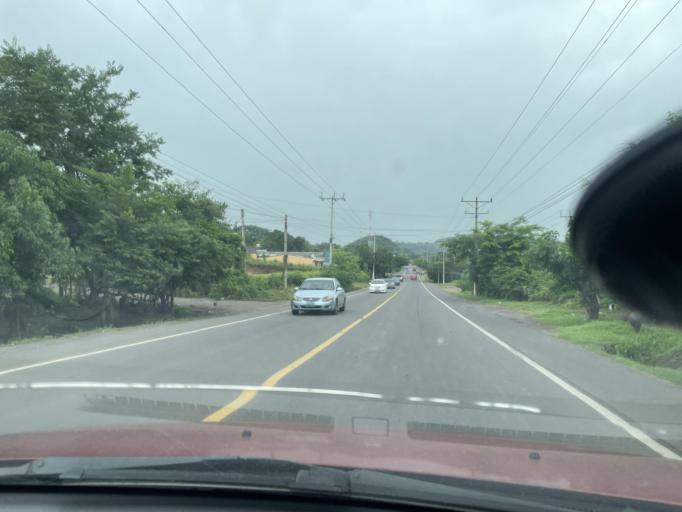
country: SV
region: San Miguel
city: San Miguel
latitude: 13.5132
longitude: -88.1478
